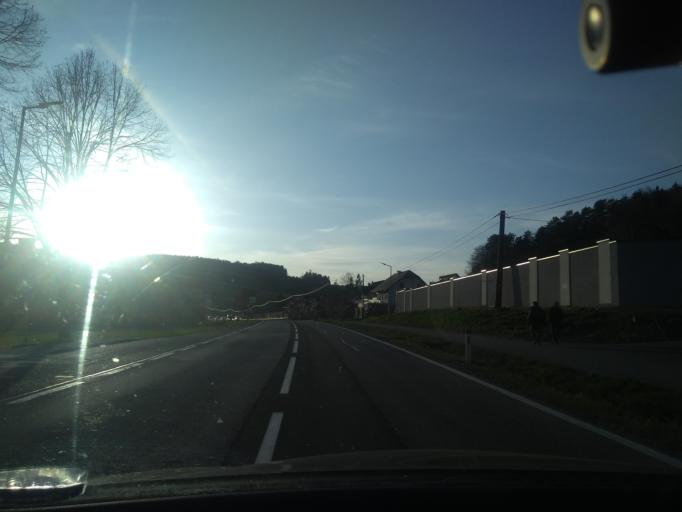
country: AT
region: Styria
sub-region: Politischer Bezirk Leibnitz
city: Heiligenkreuz am Waasen
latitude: 46.9836
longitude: 15.5572
